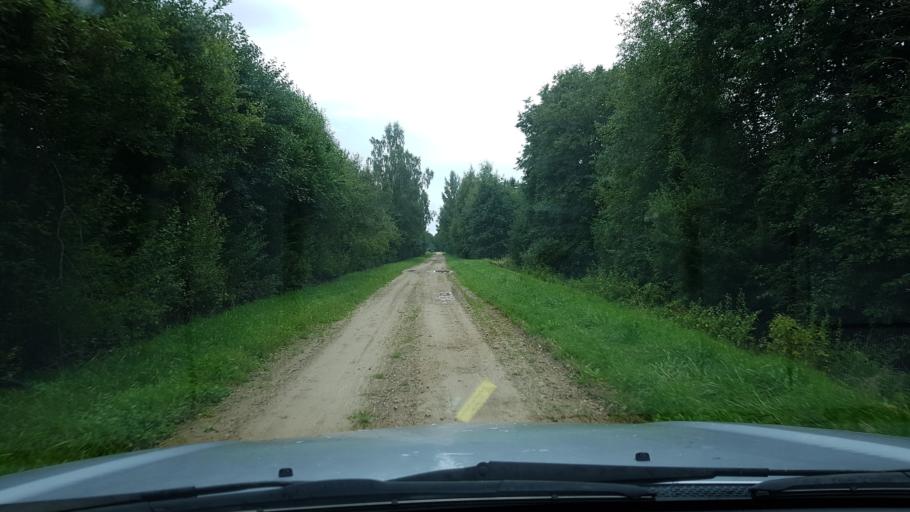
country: EE
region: Harju
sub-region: Rae vald
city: Vaida
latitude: 59.3250
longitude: 24.9385
